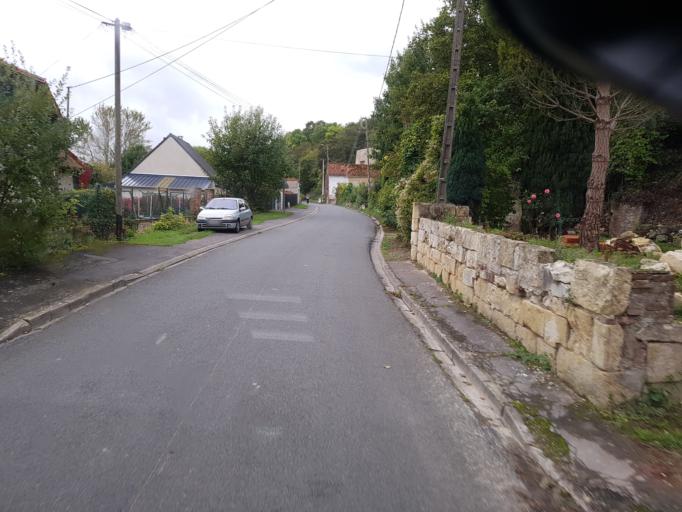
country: FR
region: Picardie
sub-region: Departement de la Somme
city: Ailly-sur-Noye
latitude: 49.6984
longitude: 2.3422
